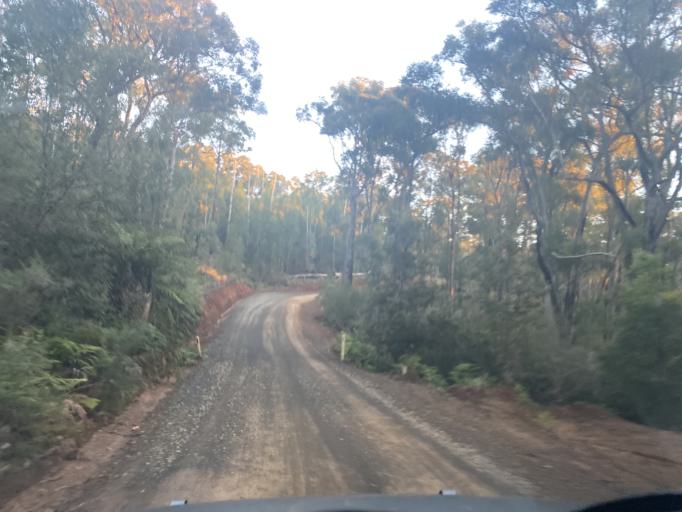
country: AU
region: Victoria
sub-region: Yarra Ranges
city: Healesville
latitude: -37.4190
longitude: 145.5278
